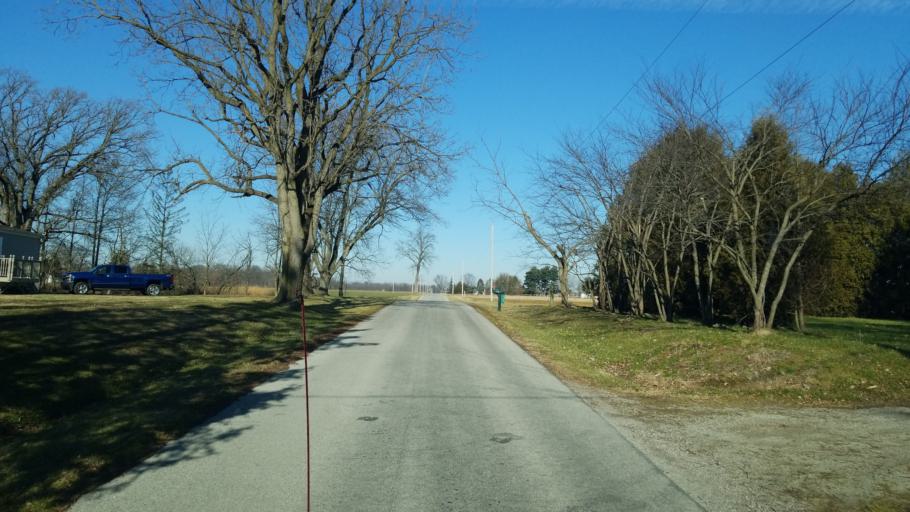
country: US
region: Ohio
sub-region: Henry County
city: Liberty Center
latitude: 41.3956
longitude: -83.9707
